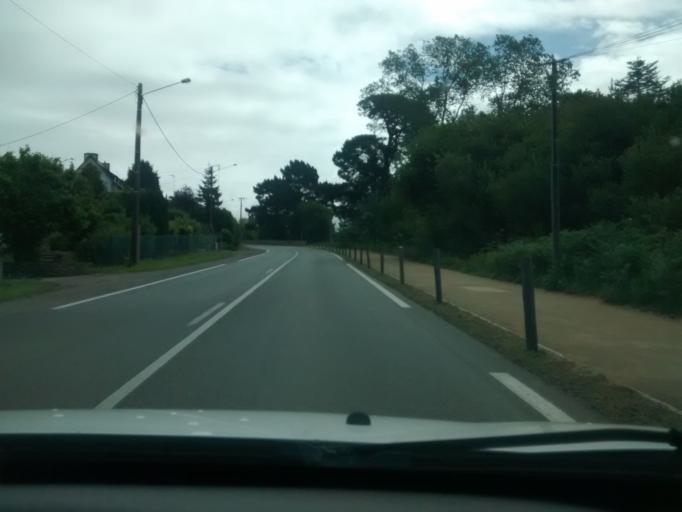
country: FR
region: Brittany
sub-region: Departement des Cotes-d'Armor
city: Louannec
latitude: 48.7952
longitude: -3.4188
